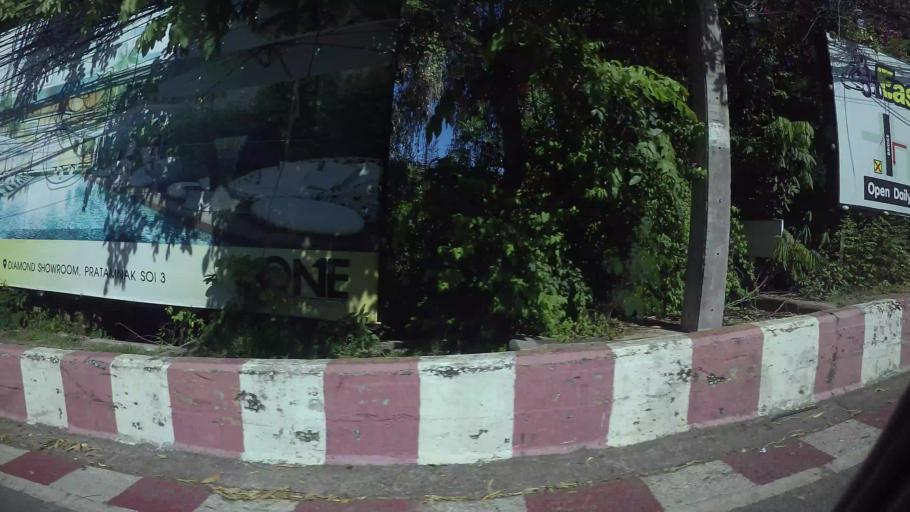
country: TH
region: Chon Buri
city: Phatthaya
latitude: 12.9189
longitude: 100.8688
